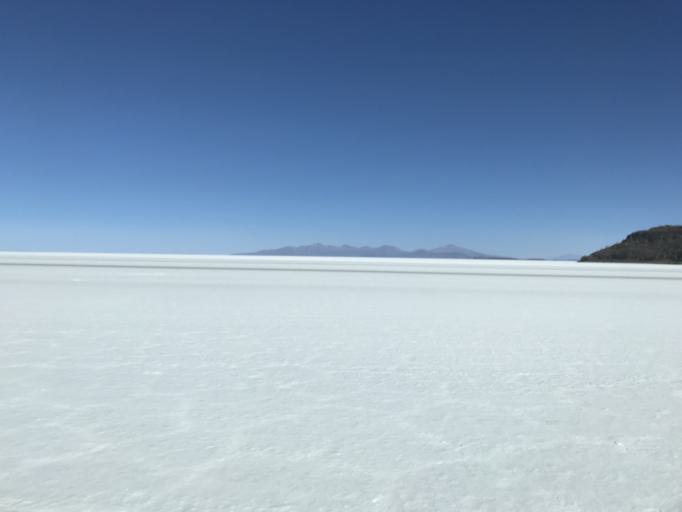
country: BO
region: Potosi
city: Colchani
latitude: -20.2382
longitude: -67.6200
